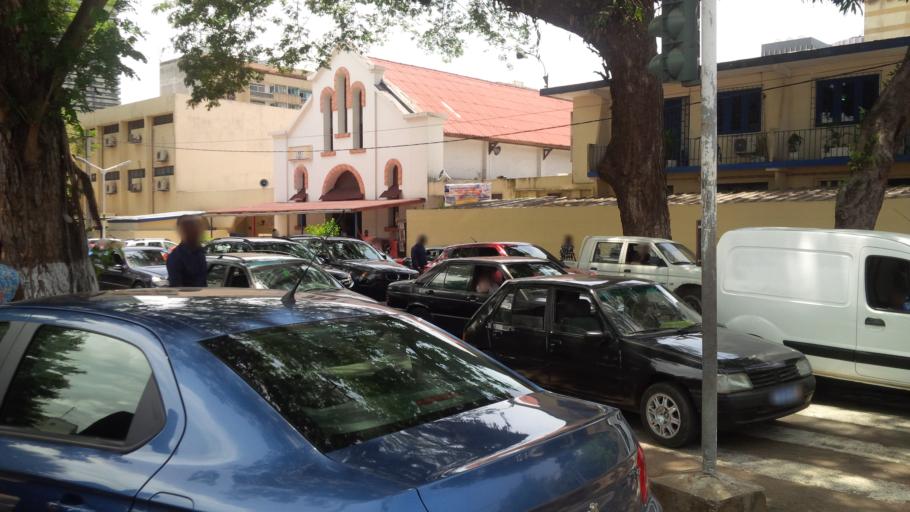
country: CI
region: Lagunes
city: Abidjan
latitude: 5.3243
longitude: -4.0219
